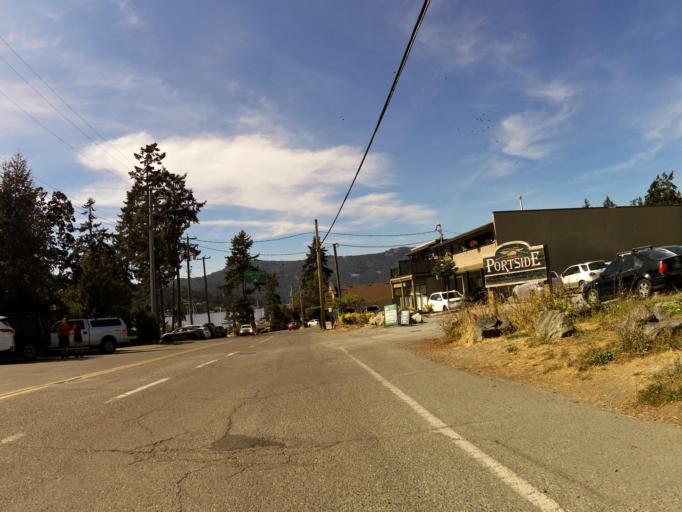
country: CA
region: British Columbia
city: North Saanich
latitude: 48.5778
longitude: -123.4645
